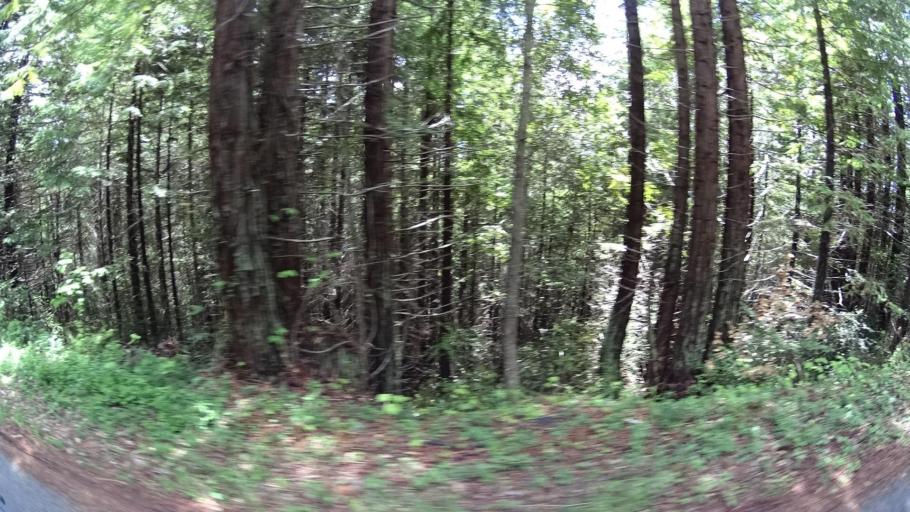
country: US
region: California
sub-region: Humboldt County
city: Blue Lake
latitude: 40.8435
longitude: -123.9179
